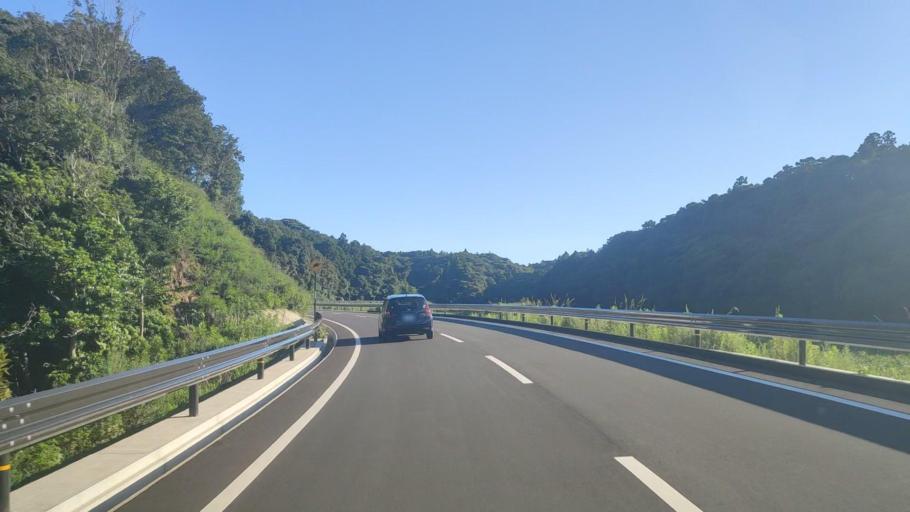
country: JP
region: Mie
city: Toba
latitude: 34.3123
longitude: 136.8816
